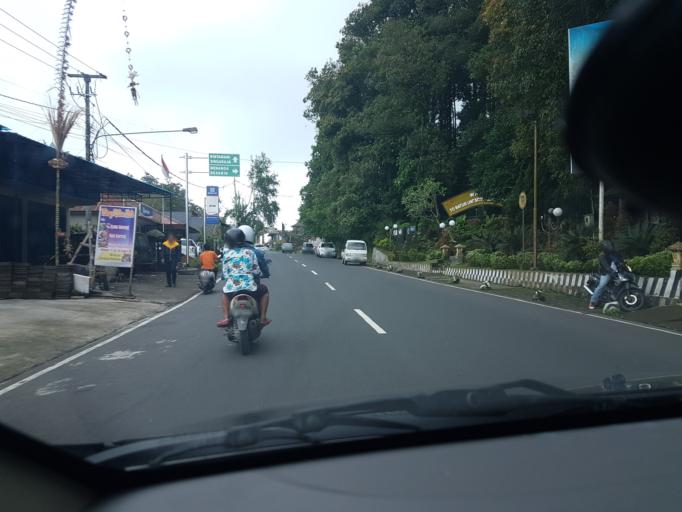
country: ID
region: Bali
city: Banjar Kedisan
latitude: -8.2856
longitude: 115.3650
